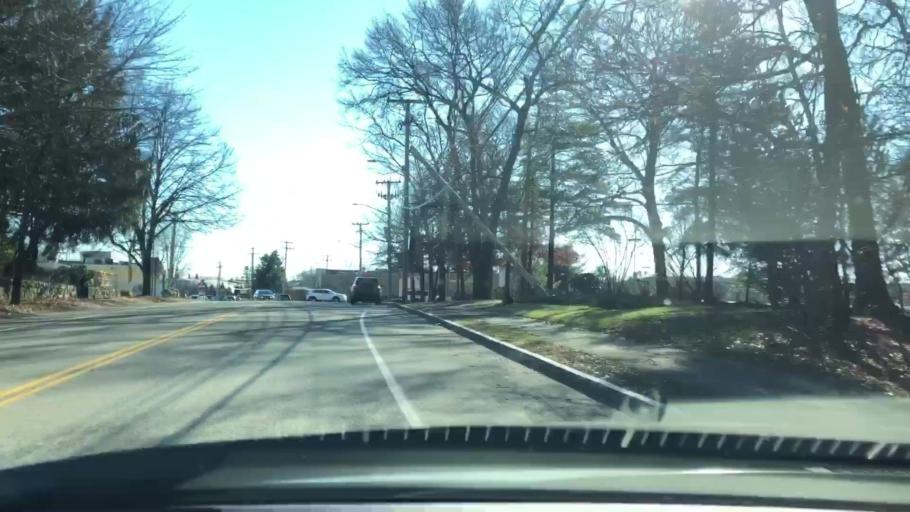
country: US
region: Massachusetts
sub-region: Norfolk County
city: Norwood
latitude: 42.1658
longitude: -71.2007
